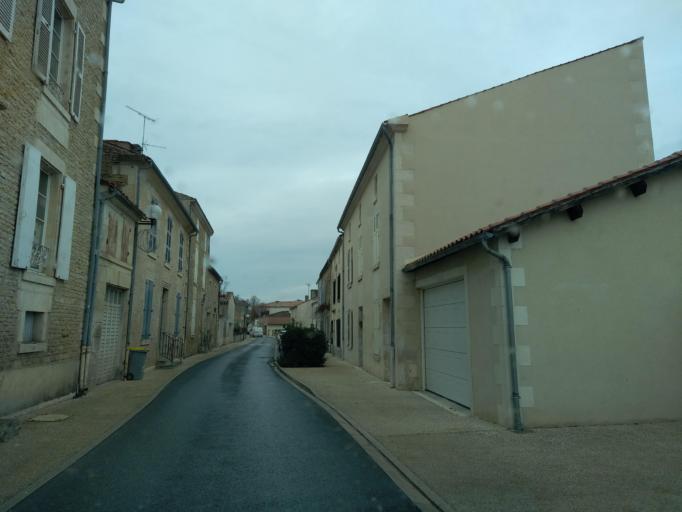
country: FR
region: Pays de la Loire
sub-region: Departement de la Vendee
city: Maillezais
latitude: 46.3725
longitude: -0.7396
